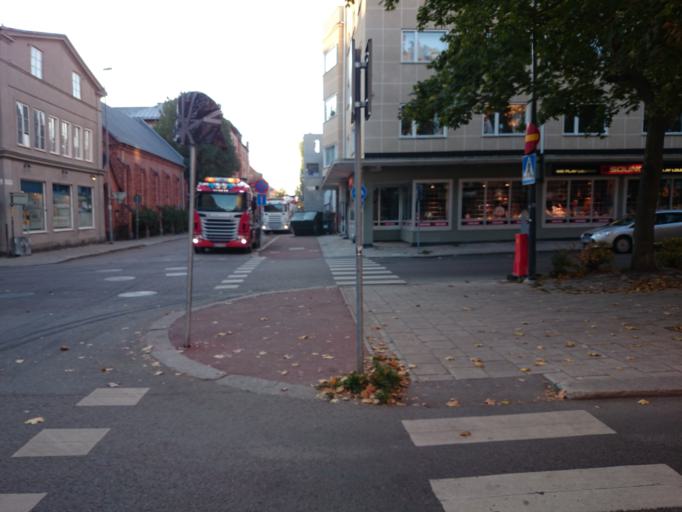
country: SE
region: Gaevleborg
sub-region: Gavle Kommun
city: Gavle
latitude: 60.6768
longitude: 17.1479
